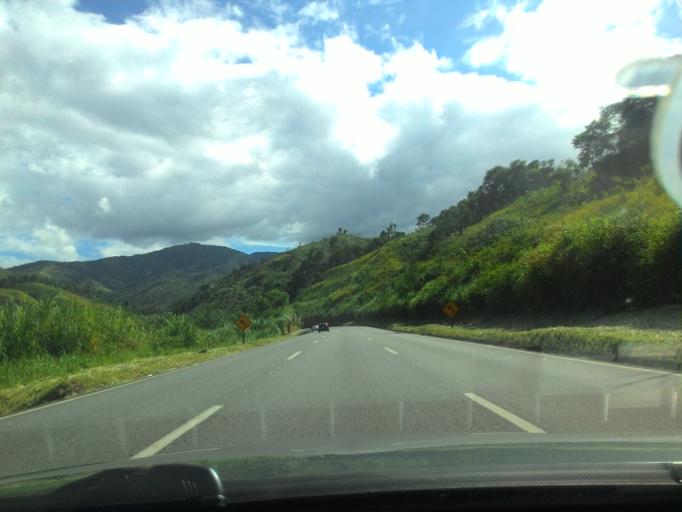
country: BR
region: Sao Paulo
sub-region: Cajati
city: Cajati
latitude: -24.8310
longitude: -48.2209
